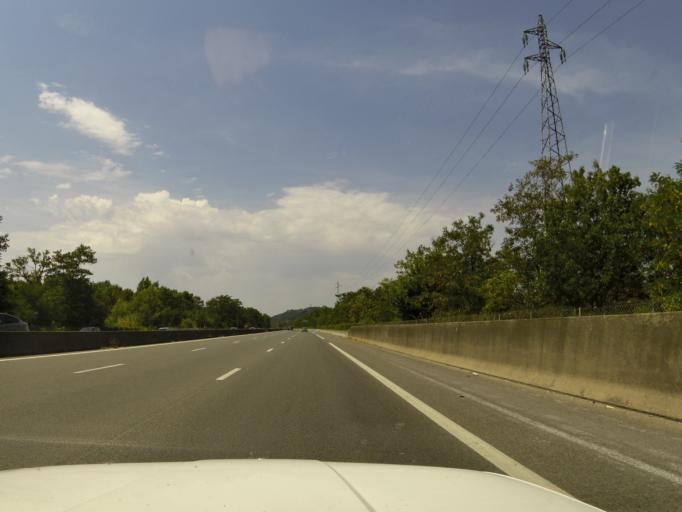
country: FR
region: Rhone-Alpes
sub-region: Departement de l'Ain
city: Miribel
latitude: 45.8153
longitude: 4.9611
